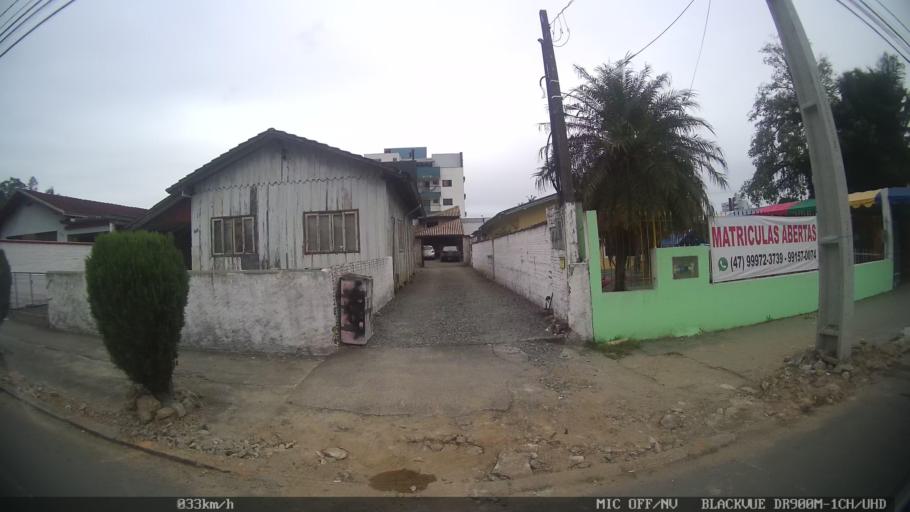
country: BR
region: Santa Catarina
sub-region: Joinville
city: Joinville
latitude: -26.2665
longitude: -48.8437
